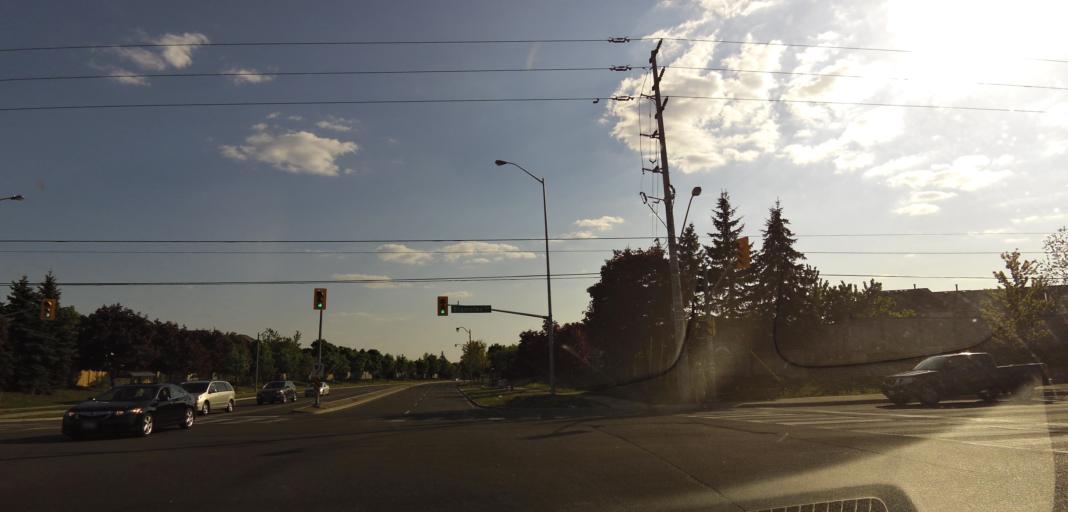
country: CA
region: Ontario
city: Brampton
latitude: 43.7542
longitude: -79.7574
